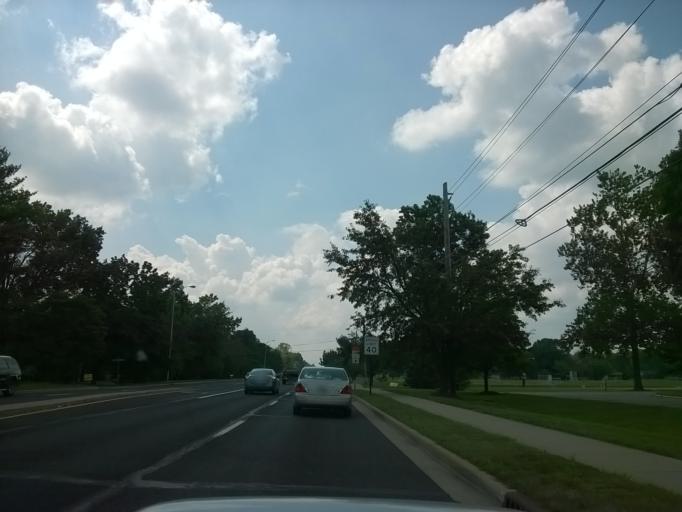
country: US
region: Indiana
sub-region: Marion County
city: Meridian Hills
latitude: 39.9127
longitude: -86.1467
